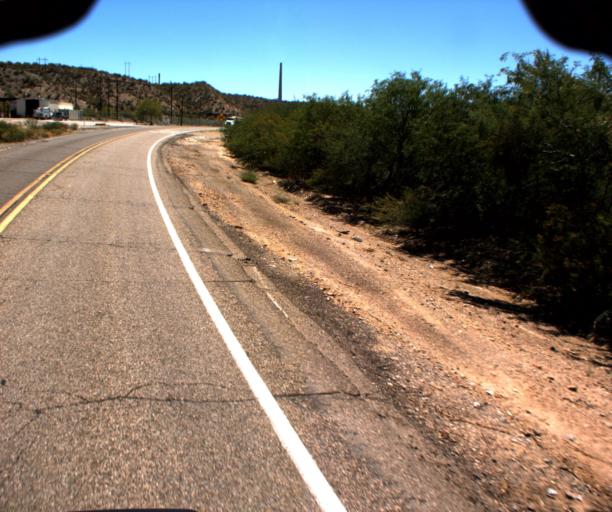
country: US
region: Arizona
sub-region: Pinal County
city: Kearny
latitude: 33.0111
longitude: -110.8121
